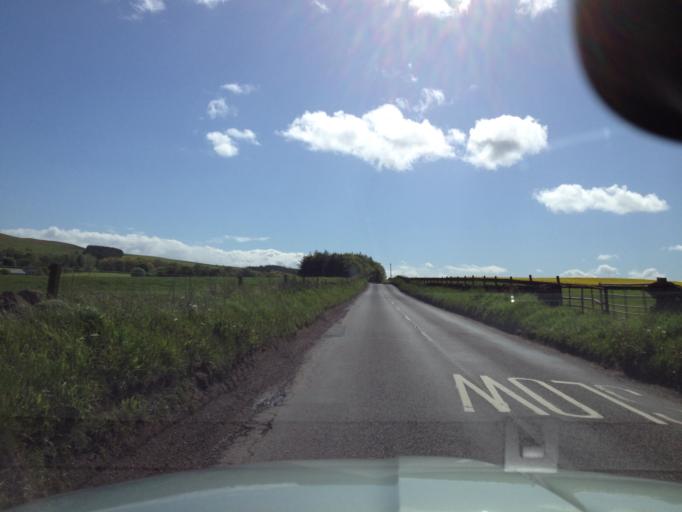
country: GB
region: Scotland
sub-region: Angus
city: Letham
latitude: 56.6854
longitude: -2.7926
